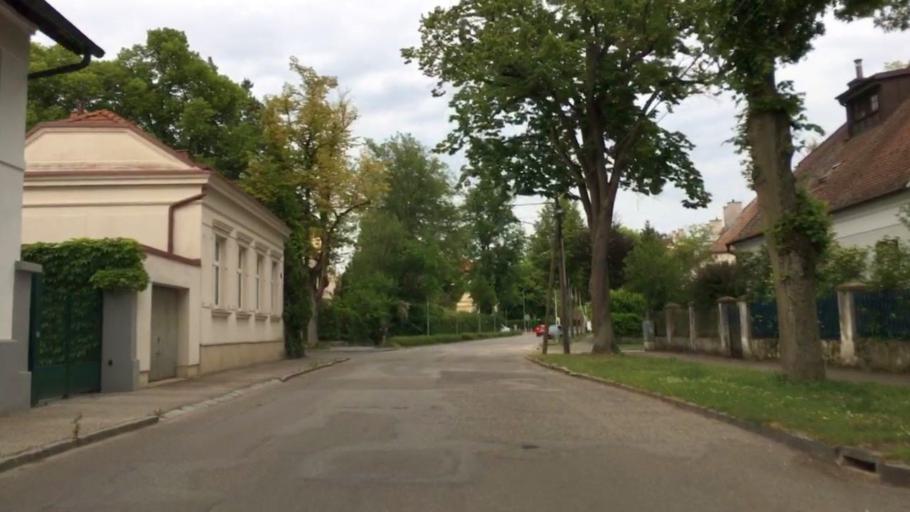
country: AT
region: Lower Austria
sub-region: Politischer Bezirk Korneuburg
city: Stockerau
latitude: 48.3894
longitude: 16.2047
